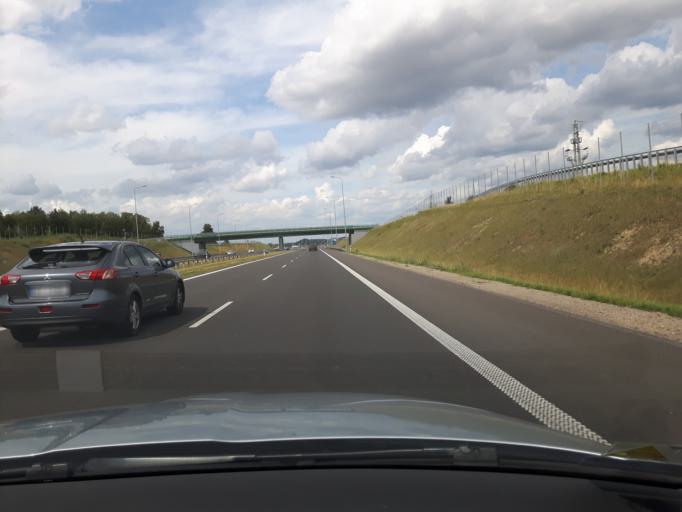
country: PL
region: Warmian-Masurian Voivodeship
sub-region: Powiat nidzicki
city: Nidzica
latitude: 53.2938
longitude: 20.4378
